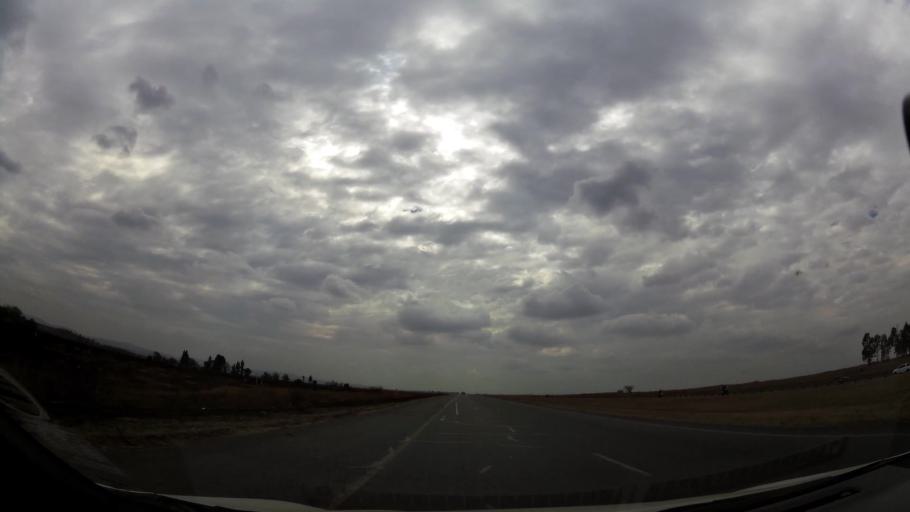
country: ZA
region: Gauteng
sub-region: Sedibeng District Municipality
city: Meyerton
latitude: -26.3993
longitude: 28.0809
